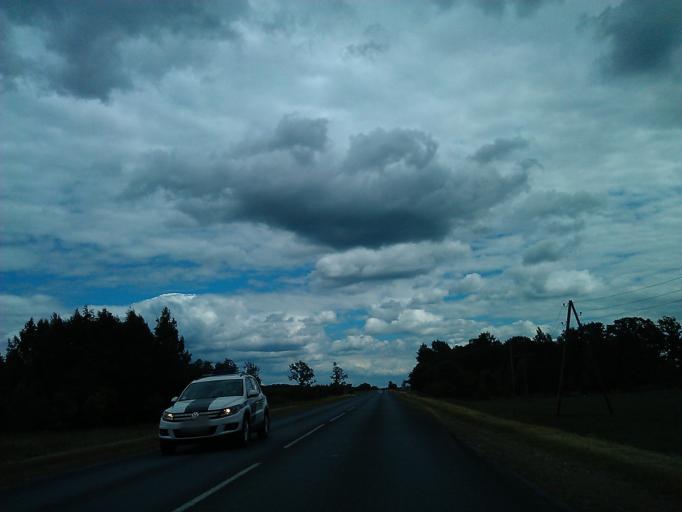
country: LV
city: Tervete
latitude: 56.6220
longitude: 23.4536
